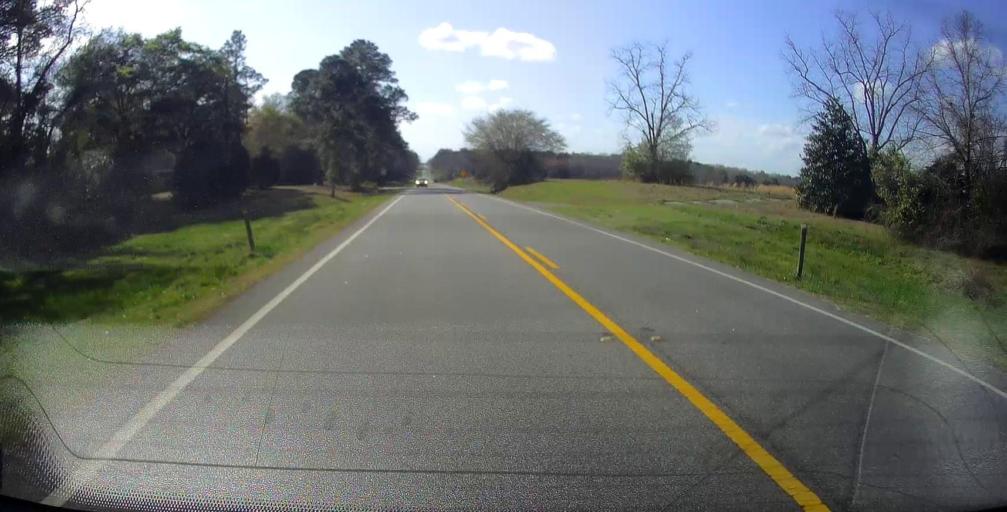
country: US
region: Georgia
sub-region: Dodge County
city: Eastman
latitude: 32.1964
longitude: -83.1905
